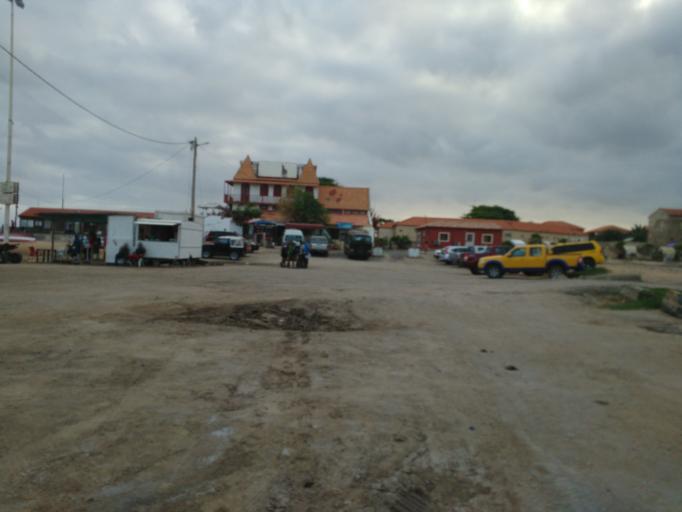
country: CV
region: Sal
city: Santa Maria
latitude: 16.5980
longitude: -22.9070
